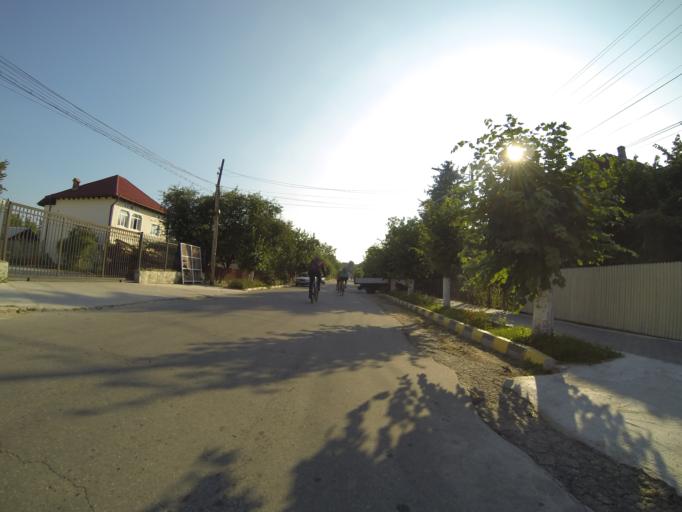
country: RO
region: Valcea
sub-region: Comuna Horezu
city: Horezu
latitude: 45.1474
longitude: 23.9952
